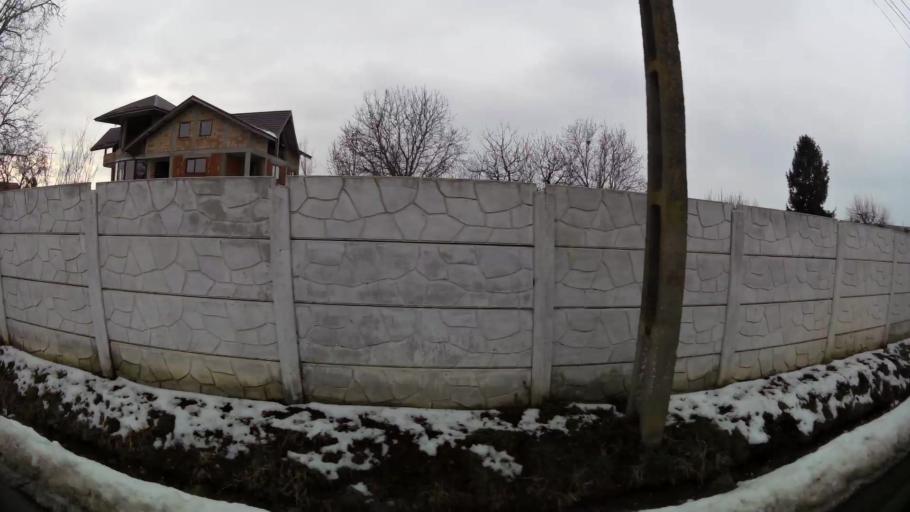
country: RO
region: Ilfov
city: Stefanestii de Jos
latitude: 44.5404
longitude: 26.2104
